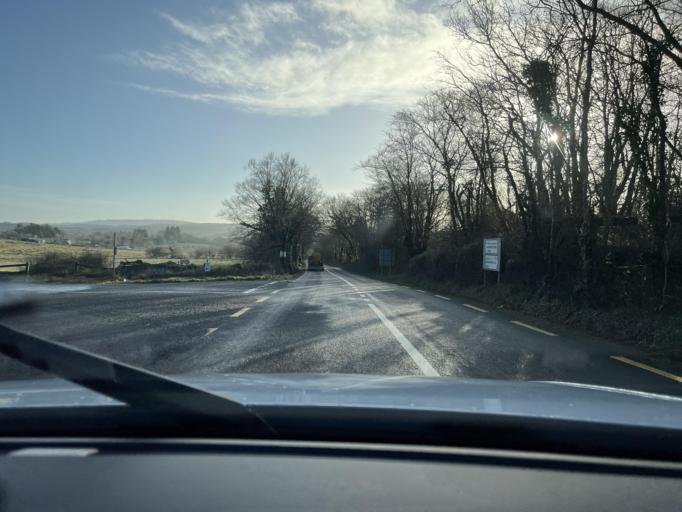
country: IE
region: Connaught
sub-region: County Leitrim
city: Manorhamilton
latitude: 54.2198
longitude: -8.2105
